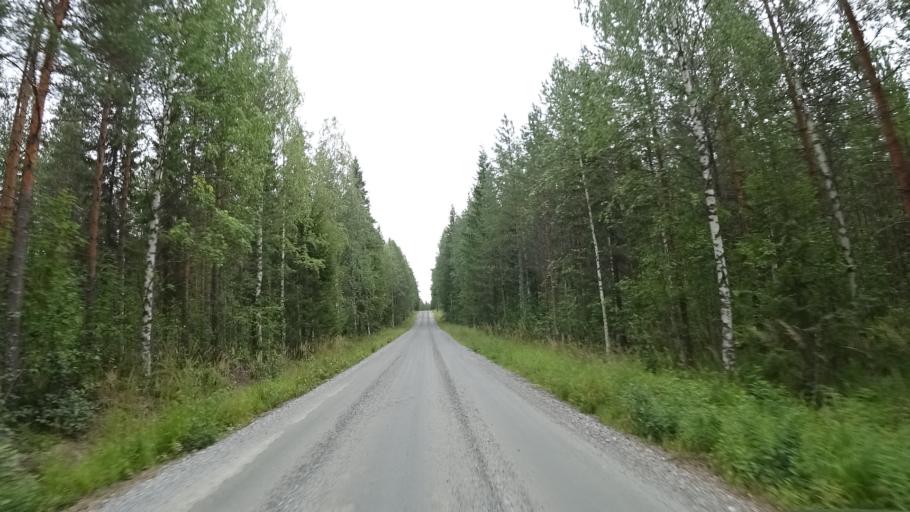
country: FI
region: North Karelia
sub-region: Pielisen Karjala
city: Lieksa
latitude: 63.3757
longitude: 30.3597
